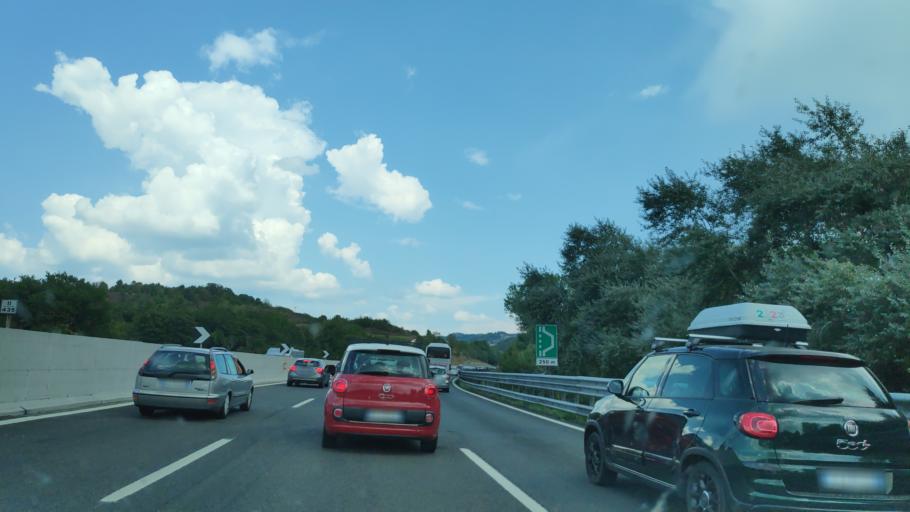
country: IT
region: Umbria
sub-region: Provincia di Terni
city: Stazione di Allerona
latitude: 42.8184
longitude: 12.0330
